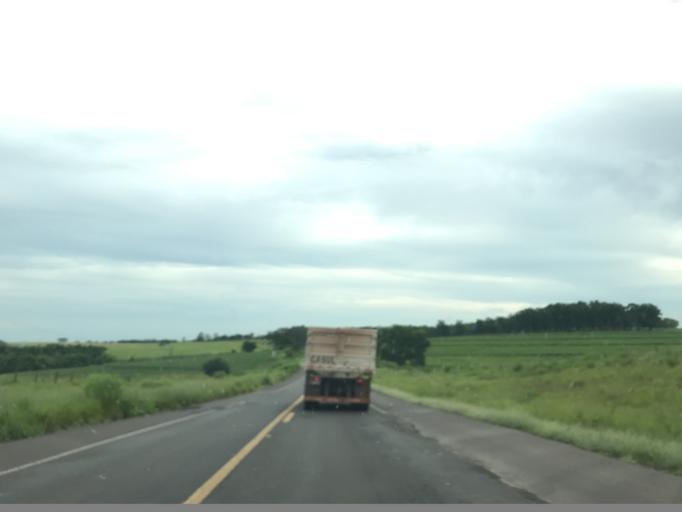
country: BR
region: Sao Paulo
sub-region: Tupa
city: Tupa
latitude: -21.6519
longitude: -50.5250
